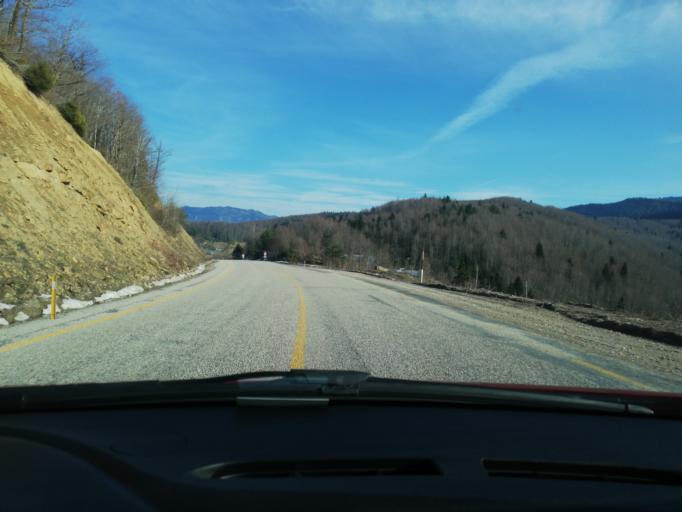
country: TR
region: Kastamonu
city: Senpazar
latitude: 41.7932
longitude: 33.1174
